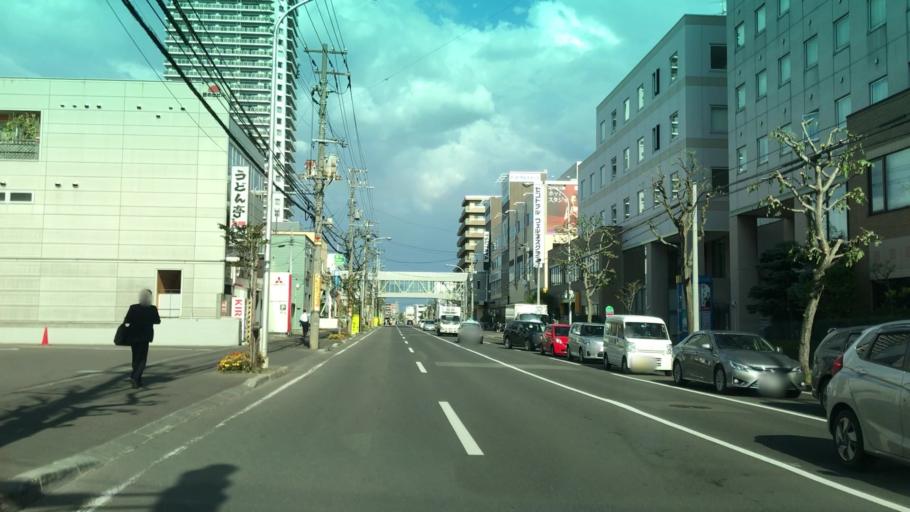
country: JP
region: Hokkaido
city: Sapporo
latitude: 43.0808
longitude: 141.3048
